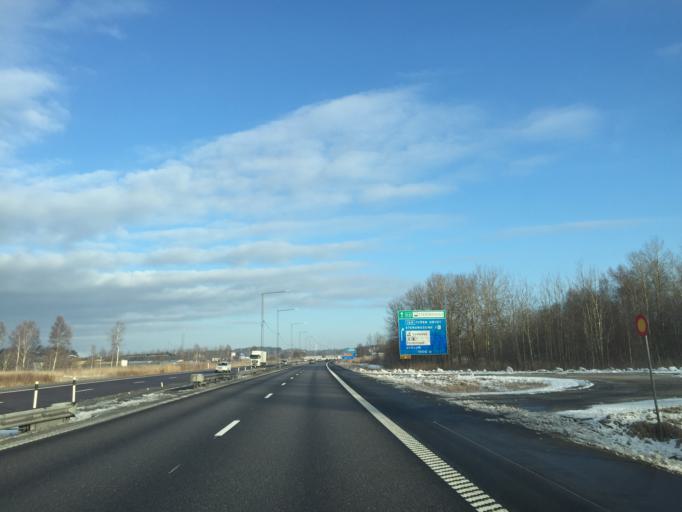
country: SE
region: Vaestra Goetaland
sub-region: Stenungsunds Kommun
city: Stora Hoga
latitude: 58.0154
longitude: 11.8436
